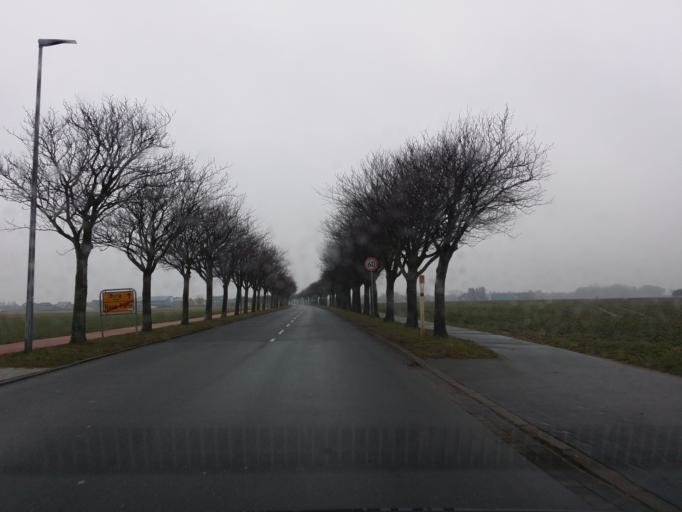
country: DE
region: Schleswig-Holstein
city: Burg auf Fehmarn
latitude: 54.4237
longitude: 11.2064
